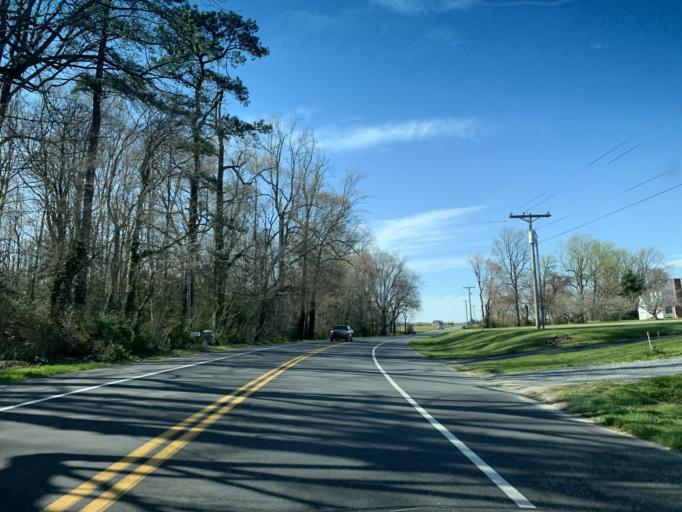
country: US
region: Delaware
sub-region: Kent County
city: Riverview
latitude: 38.9911
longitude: -75.5134
